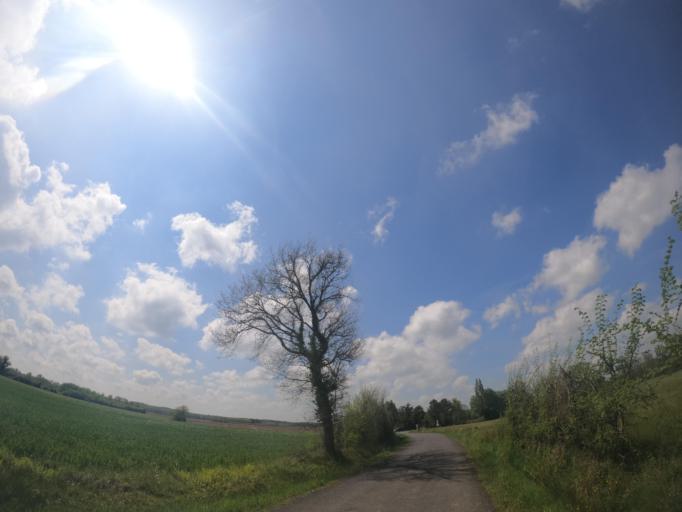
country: FR
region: Poitou-Charentes
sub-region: Departement des Deux-Sevres
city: Saint-Varent
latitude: 46.8584
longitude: -0.2263
